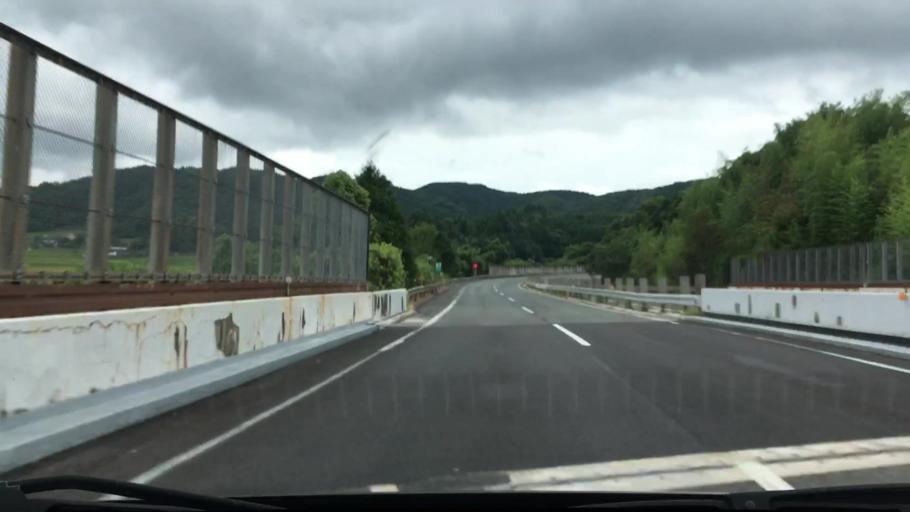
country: JP
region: Okayama
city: Niimi
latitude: 34.9068
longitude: 133.3017
